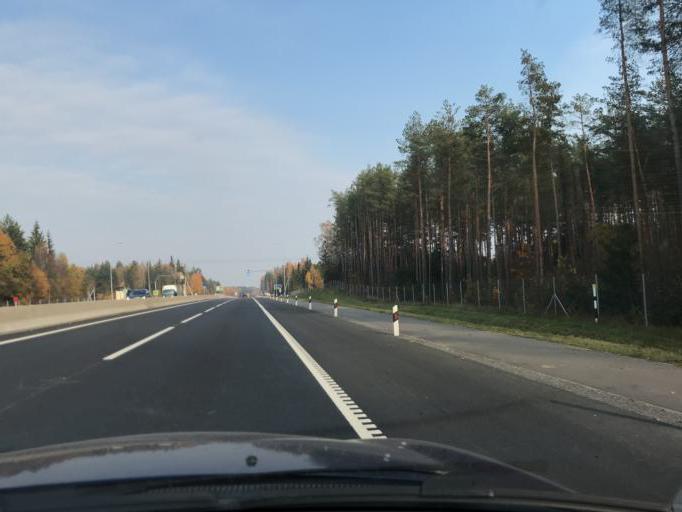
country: BY
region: Grodnenskaya
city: Shchuchin
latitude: 53.6589
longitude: 24.8083
